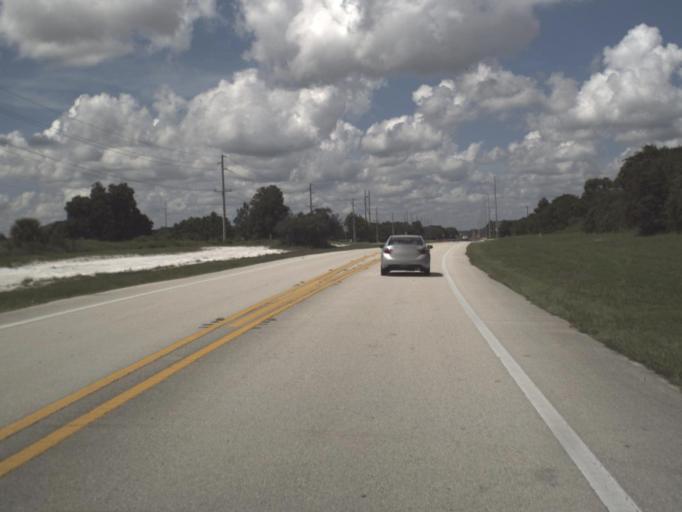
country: US
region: Florida
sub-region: Polk County
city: Combee Settlement
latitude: 28.1116
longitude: -81.9157
